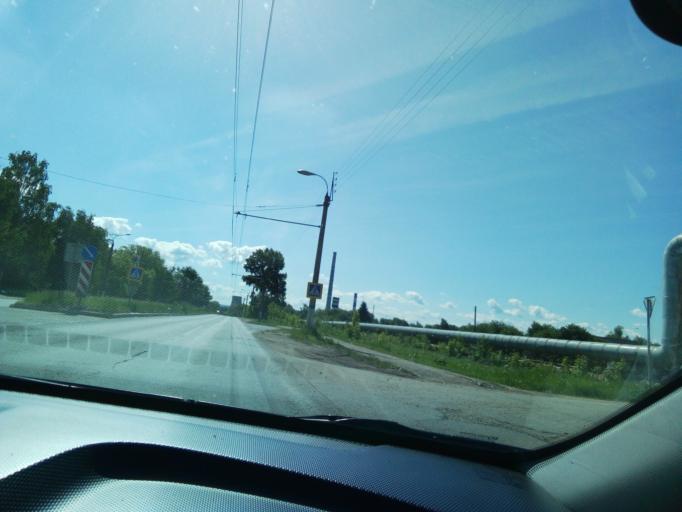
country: RU
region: Chuvashia
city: Novocheboksarsk
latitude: 56.0937
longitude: 47.4960
